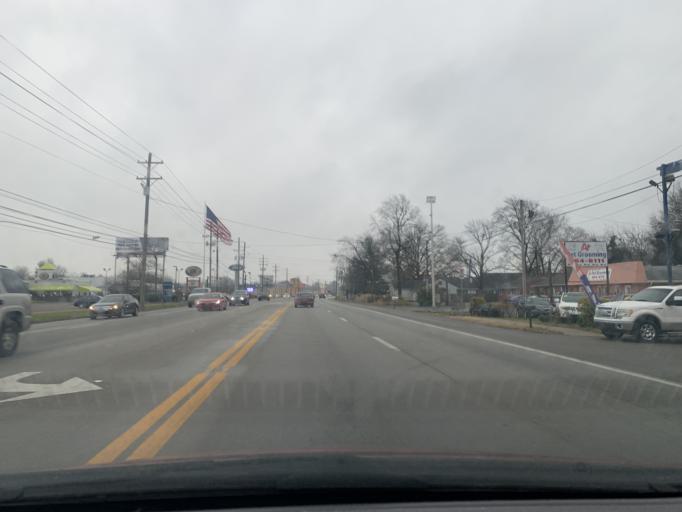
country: US
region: Kentucky
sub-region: Jefferson County
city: Okolona
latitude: 38.1648
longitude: -85.7025
